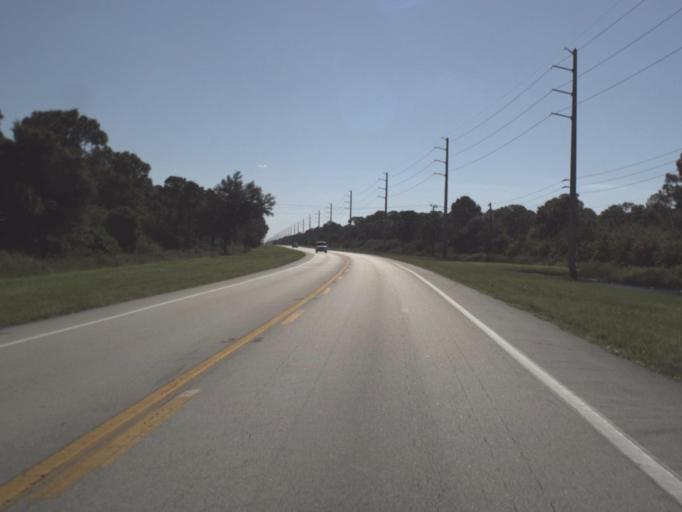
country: US
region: Florida
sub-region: Lee County
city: Gateway
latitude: 26.5918
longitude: -81.7366
